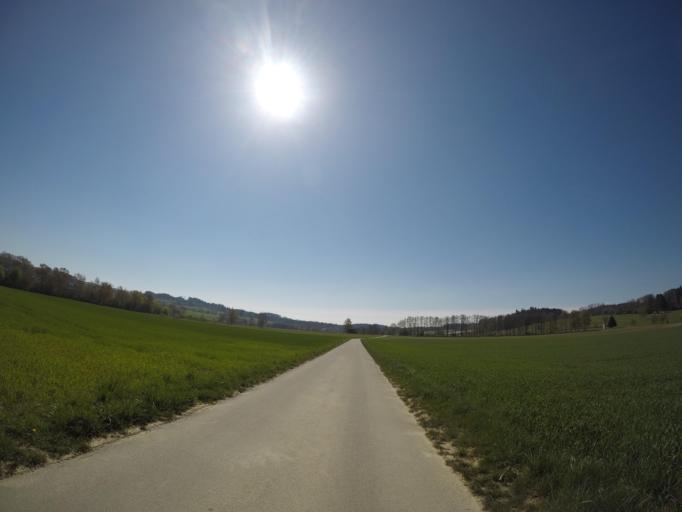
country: DE
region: Baden-Wuerttemberg
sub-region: Tuebingen Region
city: Wilhelmsdorf
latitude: 47.8328
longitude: 9.4496
